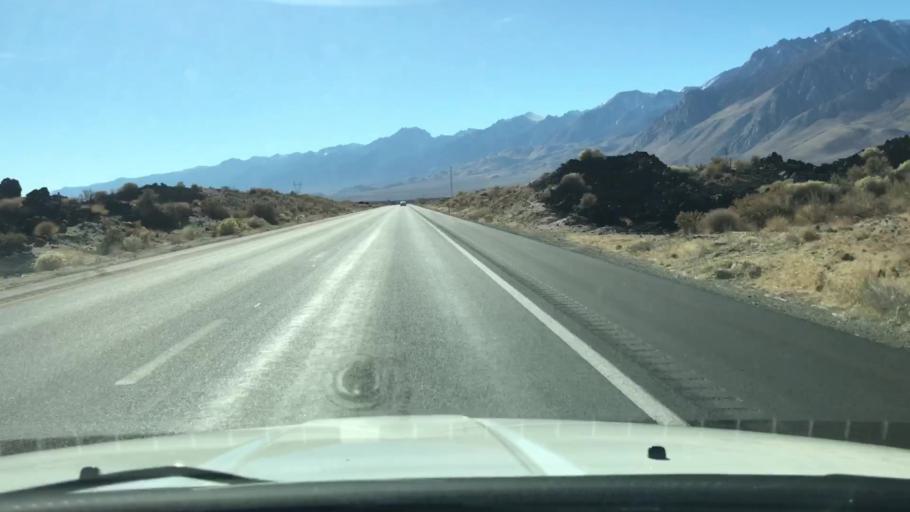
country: US
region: California
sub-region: Inyo County
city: Big Pine
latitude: 36.9865
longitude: -118.2354
